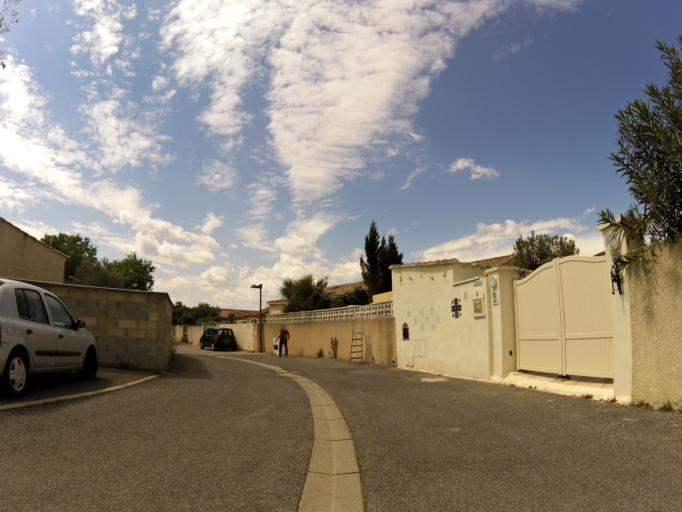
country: FR
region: Languedoc-Roussillon
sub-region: Departement du Gard
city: Gallargues-le-Montueux
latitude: 43.7217
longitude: 4.1646
